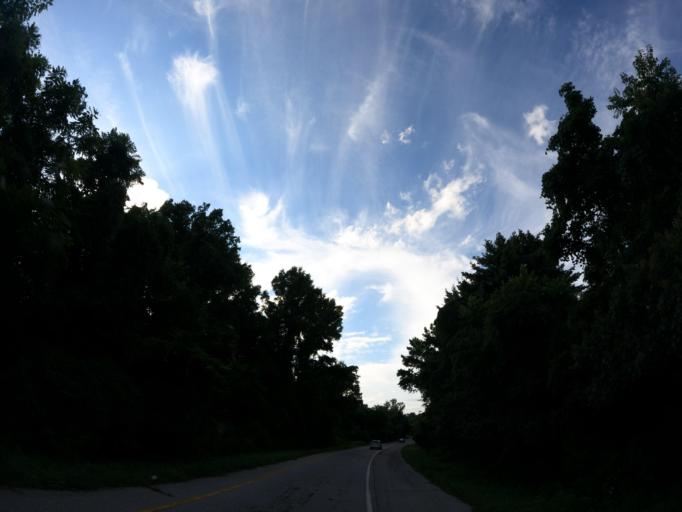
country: US
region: Maryland
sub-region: Howard County
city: Columbia
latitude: 39.2249
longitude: -76.8426
